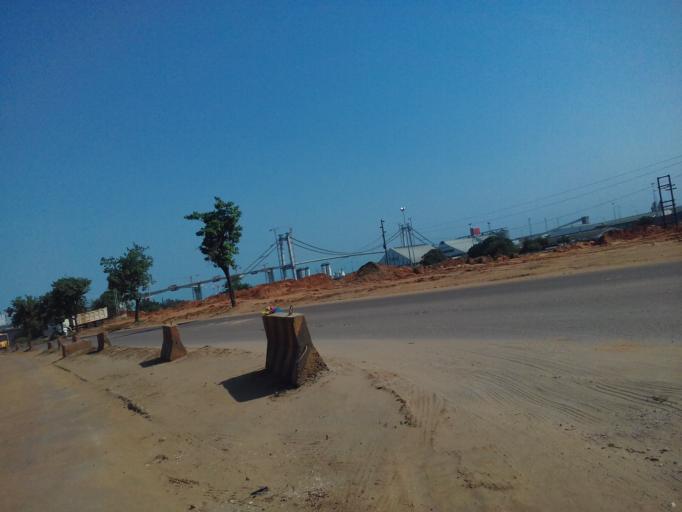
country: MZ
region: Maputo City
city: Maputo
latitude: -25.9565
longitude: 32.5531
